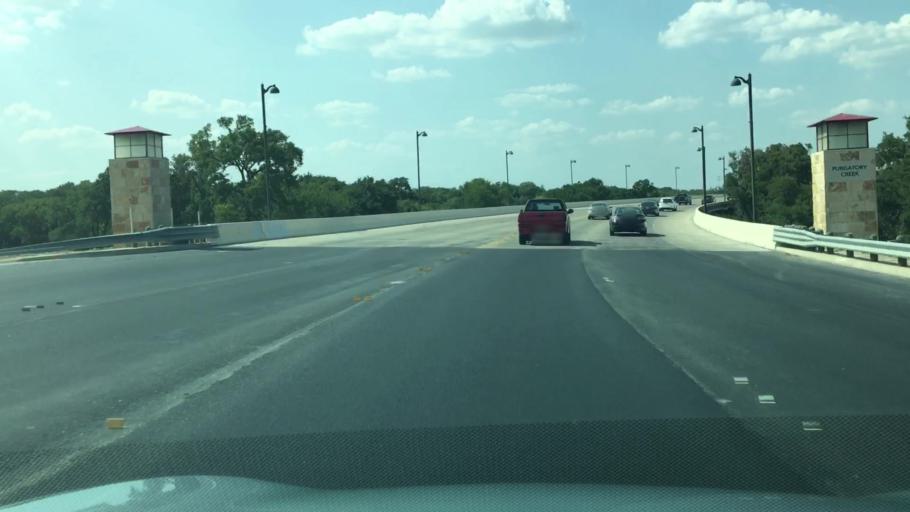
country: US
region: Texas
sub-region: Hays County
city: San Marcos
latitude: 29.8675
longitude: -97.9652
